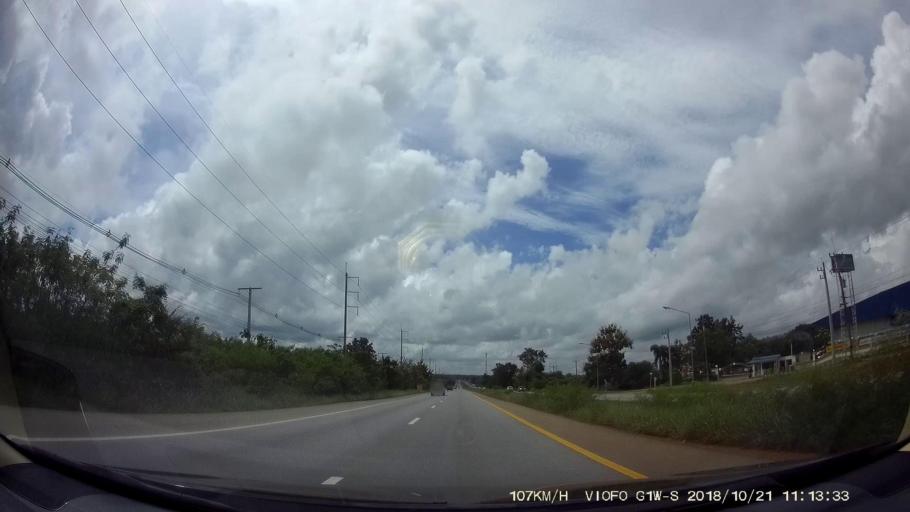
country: TH
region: Chaiyaphum
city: Chaiyaphum
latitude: 15.9150
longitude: 102.1318
